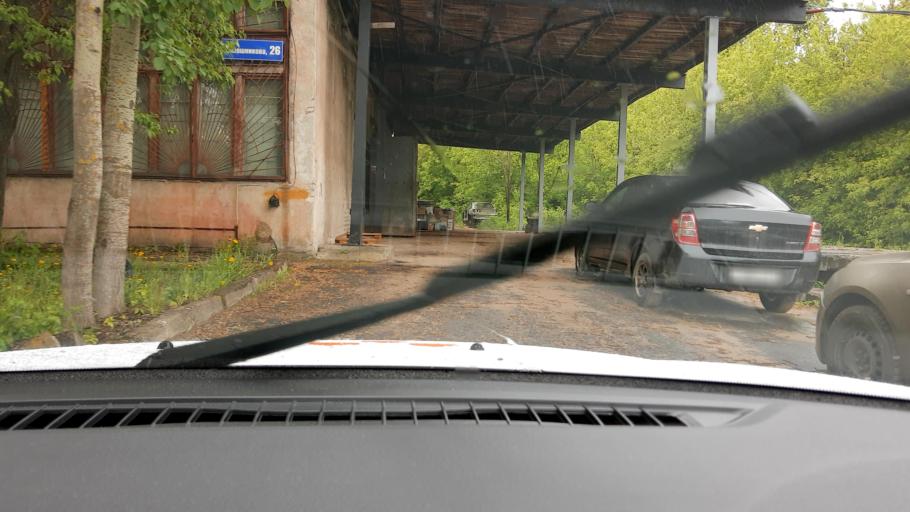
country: RU
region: Nizjnij Novgorod
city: Nizhniy Novgorod
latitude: 56.2463
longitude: 43.9990
